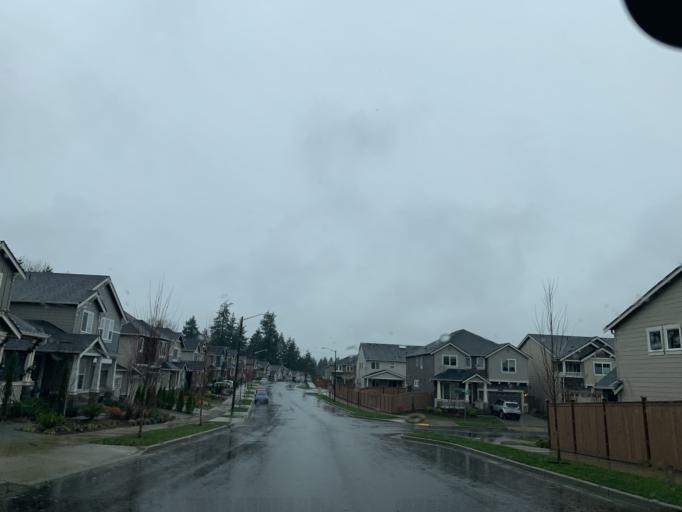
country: US
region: Washington
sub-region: King County
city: Kingsgate
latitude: 47.7370
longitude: -122.1706
